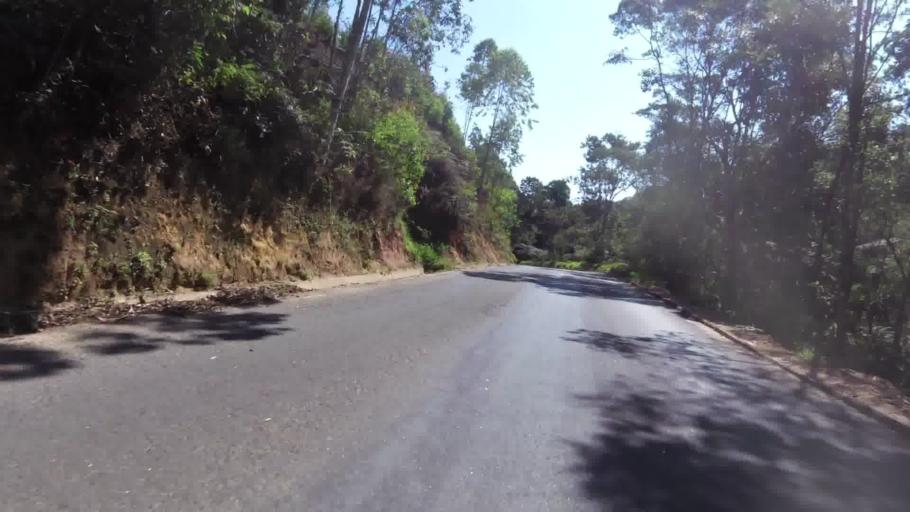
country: BR
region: Espirito Santo
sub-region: Marechal Floriano
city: Marechal Floriano
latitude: -20.4579
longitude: -40.9039
